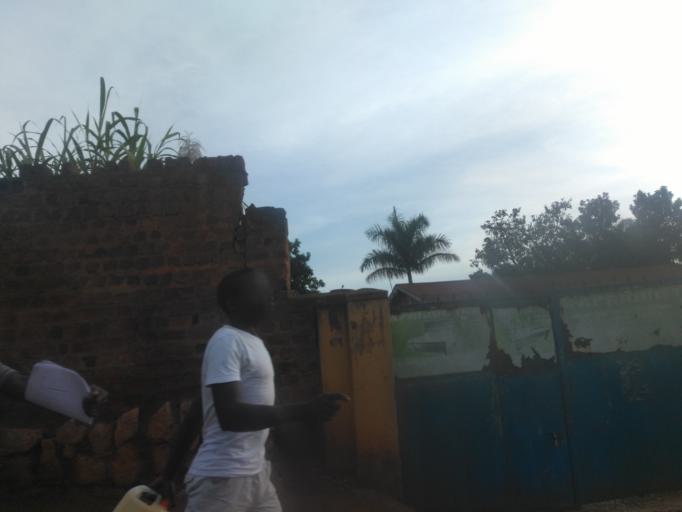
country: UG
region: Central Region
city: Kampala Central Division
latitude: 0.3477
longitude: 32.5729
